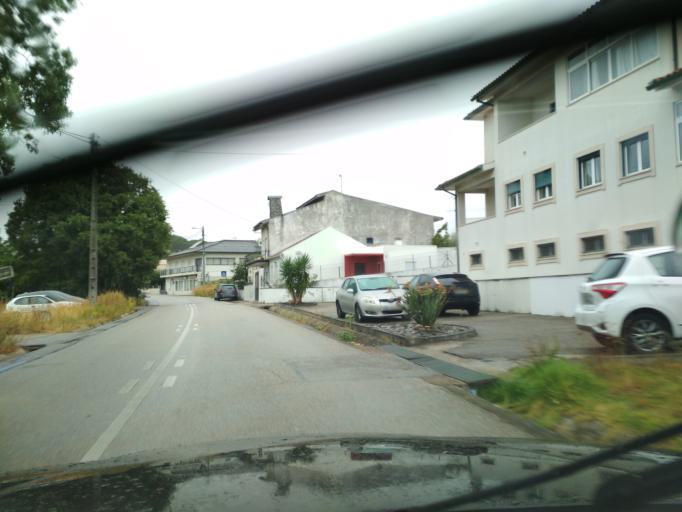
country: PT
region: Coimbra
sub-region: Coimbra
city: Coimbra
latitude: 40.1860
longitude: -8.4407
